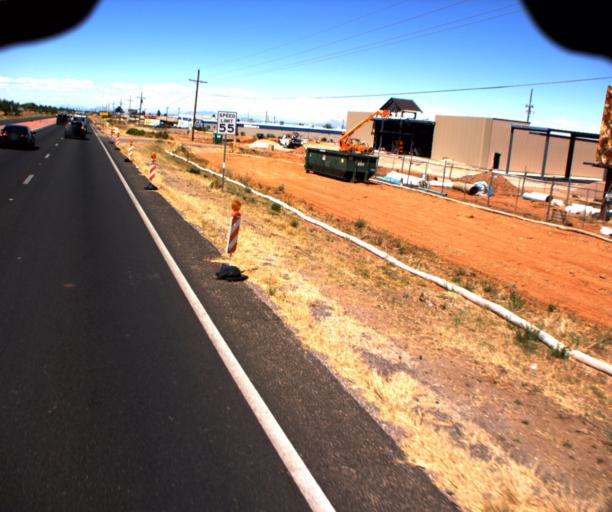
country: US
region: Arizona
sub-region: Cochise County
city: Sierra Vista Southeast
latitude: 31.4972
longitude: -110.2573
